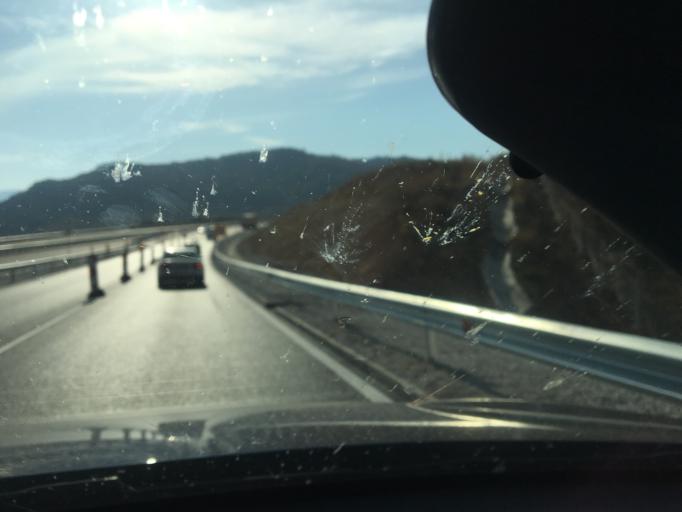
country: BG
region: Lovech
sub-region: Obshtina Yablanitsa
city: Yablanitsa
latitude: 43.0547
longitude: 24.2210
